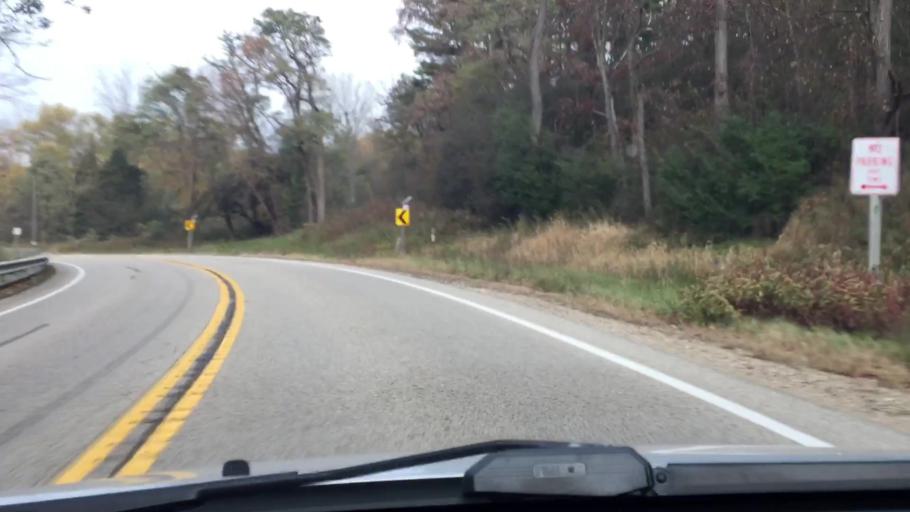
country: US
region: Wisconsin
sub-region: Waukesha County
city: Eagle
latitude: 42.9371
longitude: -88.4672
